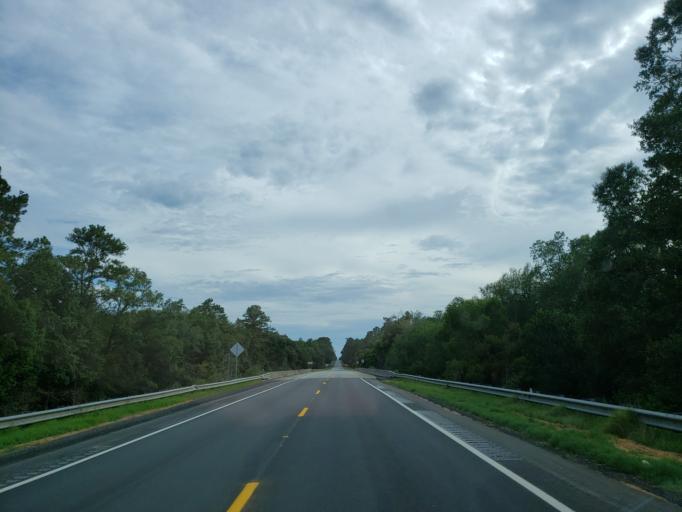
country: US
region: Georgia
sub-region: Tift County
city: Tifton
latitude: 31.5335
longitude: -83.3981
